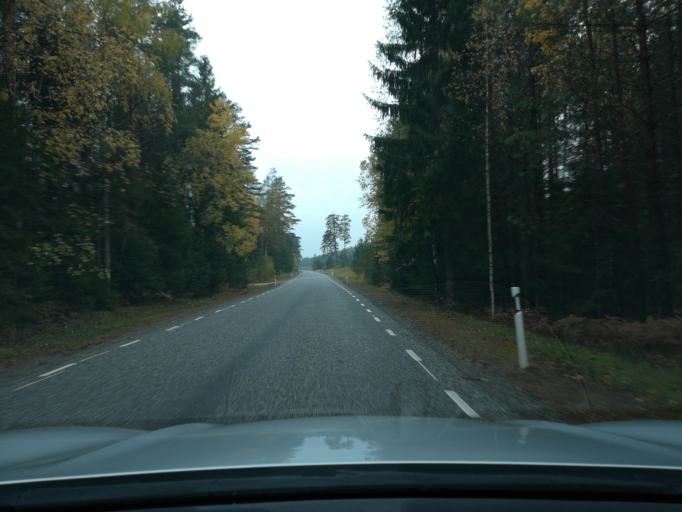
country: EE
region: Ida-Virumaa
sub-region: Johvi vald
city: Johvi
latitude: 59.1656
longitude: 27.4327
